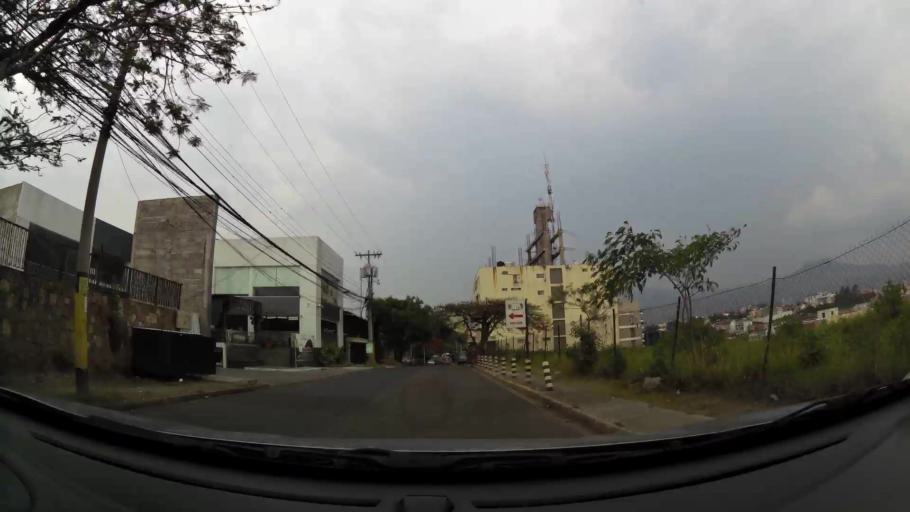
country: HN
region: Francisco Morazan
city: Tegucigalpa
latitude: 14.0929
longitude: -87.1810
